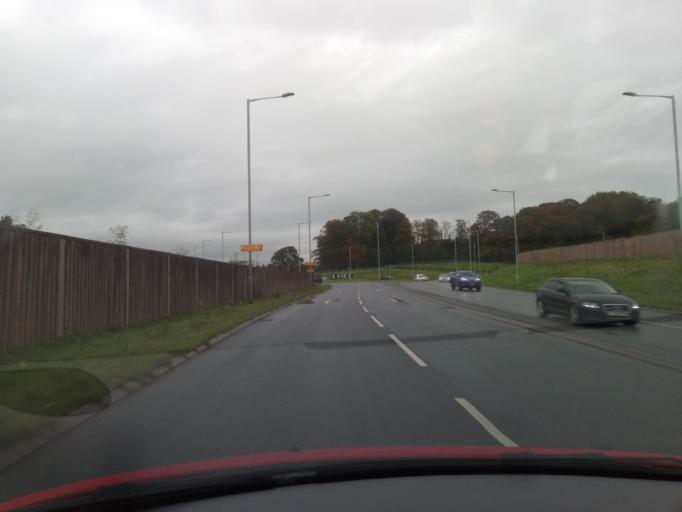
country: GB
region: England
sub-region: Lancashire
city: Preston
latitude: 53.8031
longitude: -2.7159
